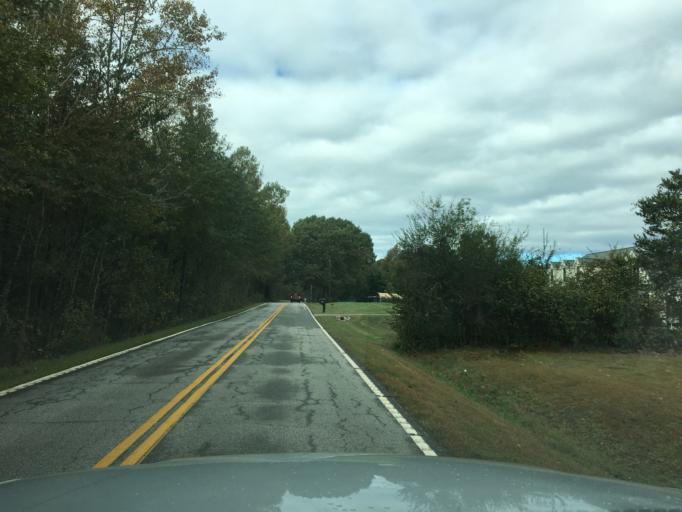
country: US
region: South Carolina
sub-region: Greenville County
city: Tigerville
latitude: 35.0610
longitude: -82.2715
